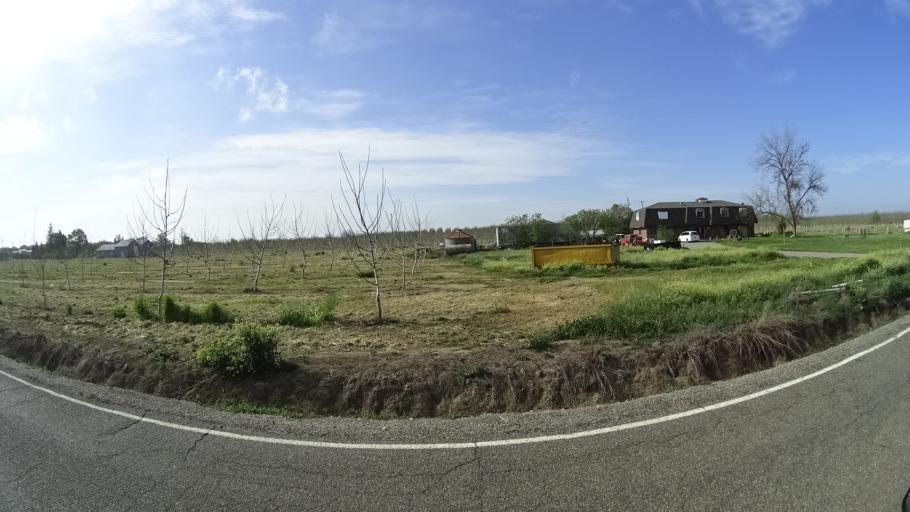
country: US
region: California
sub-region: Glenn County
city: Hamilton City
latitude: 39.6307
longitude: -122.0099
